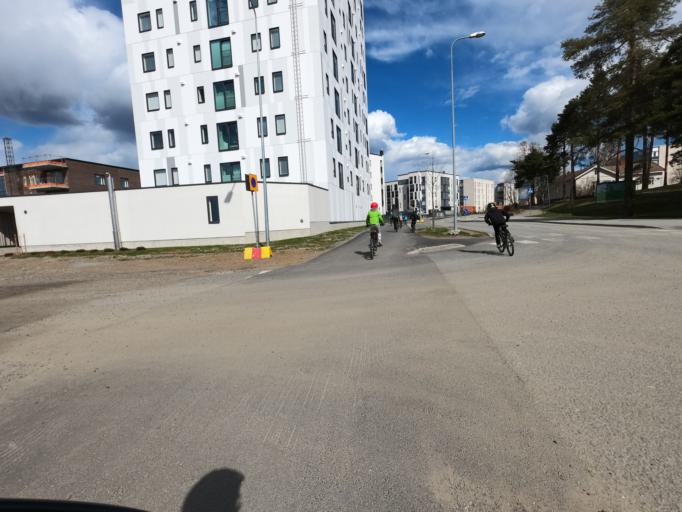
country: FI
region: North Karelia
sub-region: Joensuu
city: Joensuu
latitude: 62.5923
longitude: 29.7597
